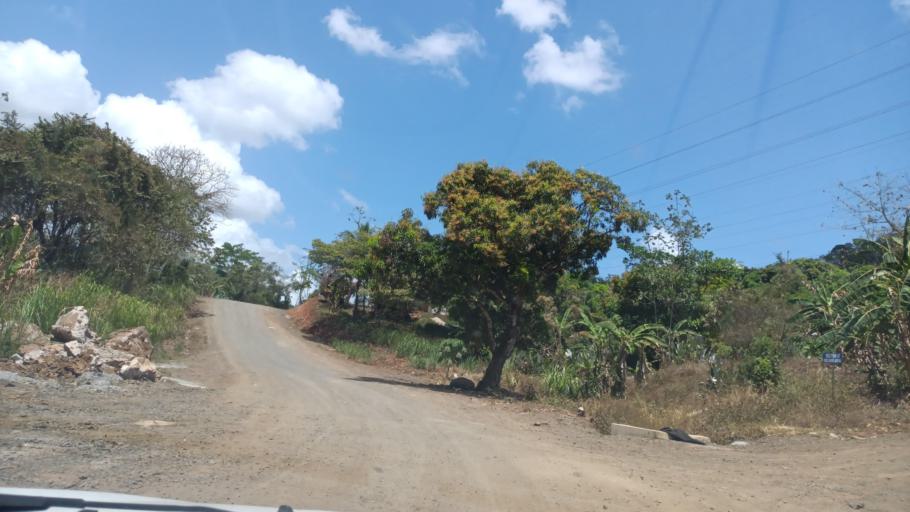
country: PA
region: Panama
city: Alcalde Diaz
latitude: 9.0803
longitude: -79.5753
